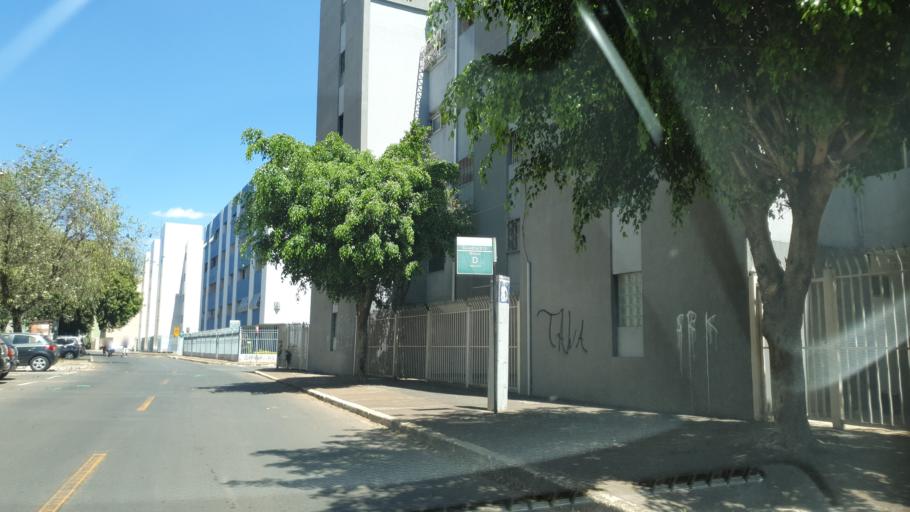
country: BR
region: Federal District
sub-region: Brasilia
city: Brasilia
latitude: -15.7934
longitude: -47.9368
